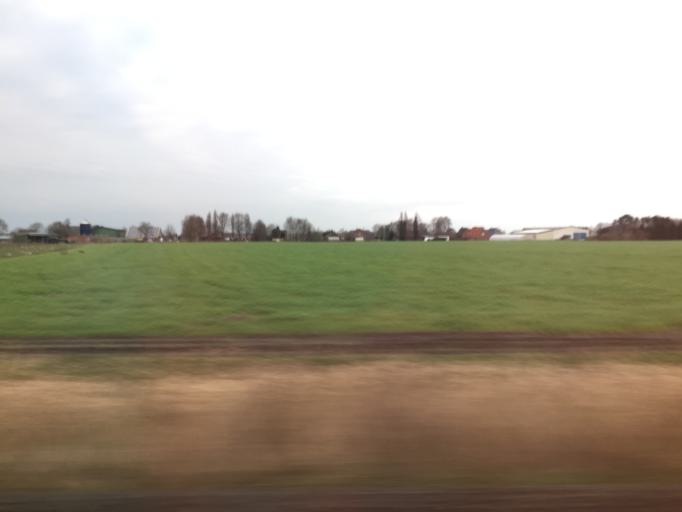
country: DE
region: Schleswig-Holstein
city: Herzhorn
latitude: 53.7814
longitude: 9.4657
